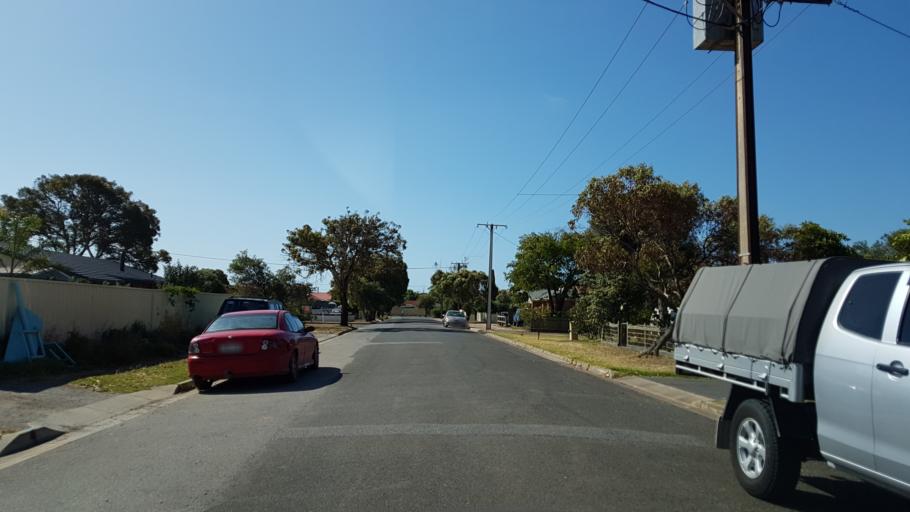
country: AU
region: South Australia
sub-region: Onkaparinga
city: Port Willunga
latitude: -35.2777
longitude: 138.4495
